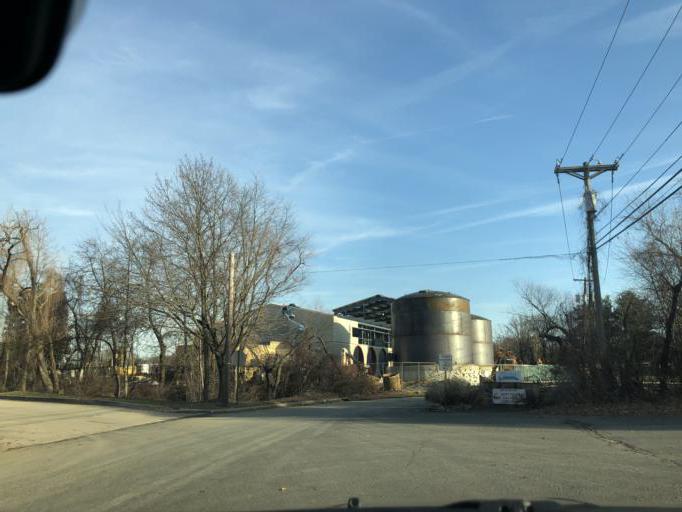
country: US
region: New Jersey
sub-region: Burlington County
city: Cinnaminson
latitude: 39.9752
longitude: -74.9880
